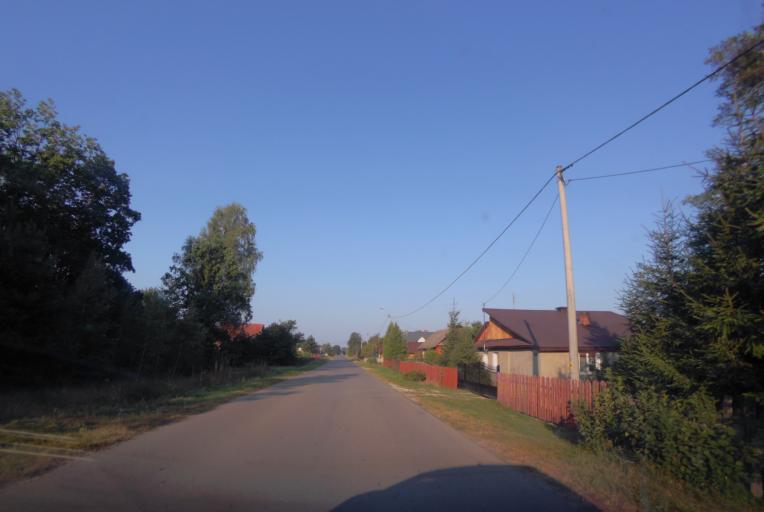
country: PL
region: Lublin Voivodeship
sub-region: Powiat janowski
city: Dzwola
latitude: 50.5833
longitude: 22.5767
